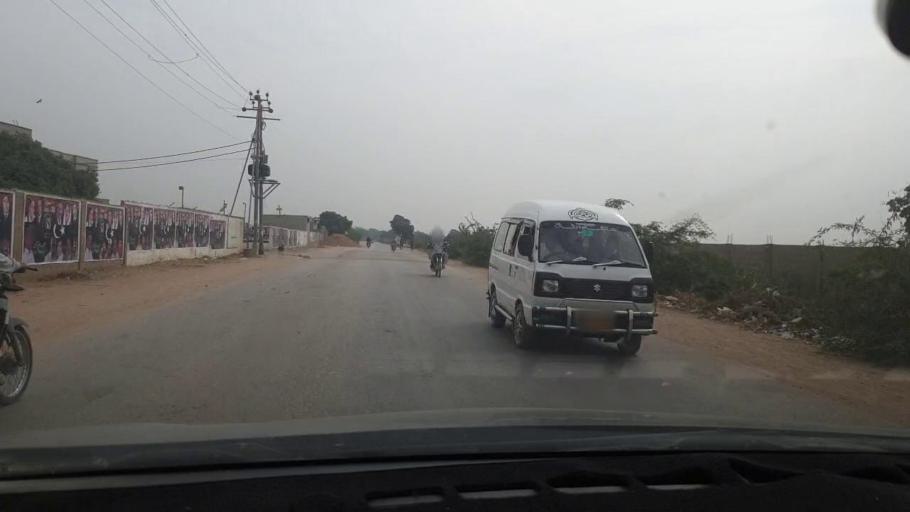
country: PK
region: Sindh
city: Malir Cantonment
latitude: 24.9174
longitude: 67.2594
